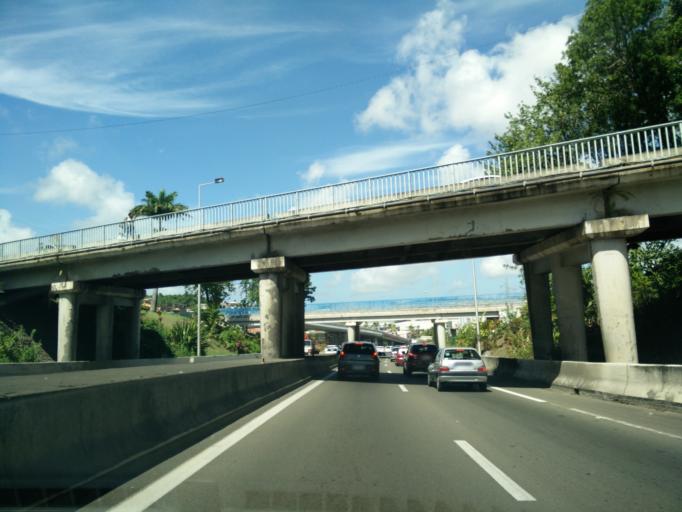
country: MQ
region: Martinique
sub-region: Martinique
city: Le Lamentin
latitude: 14.6179
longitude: -61.0398
